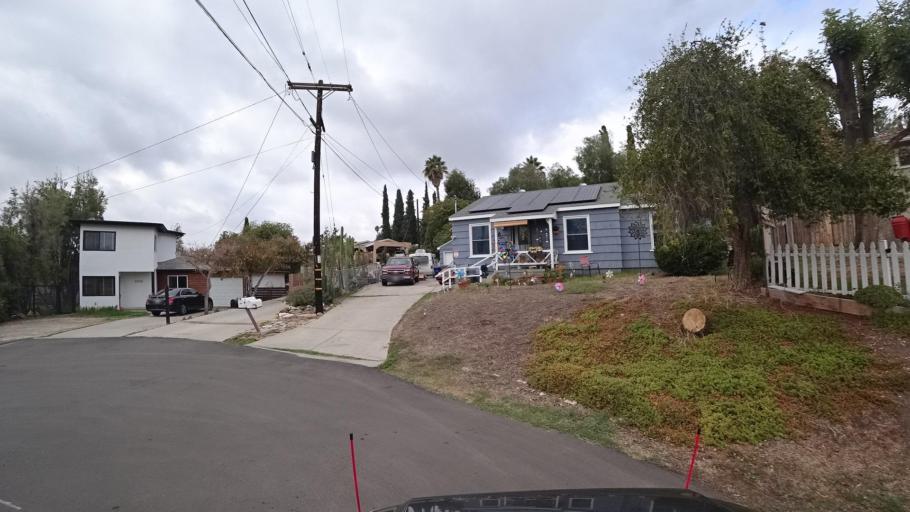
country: US
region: California
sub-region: San Diego County
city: Spring Valley
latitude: 32.7433
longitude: -117.0059
